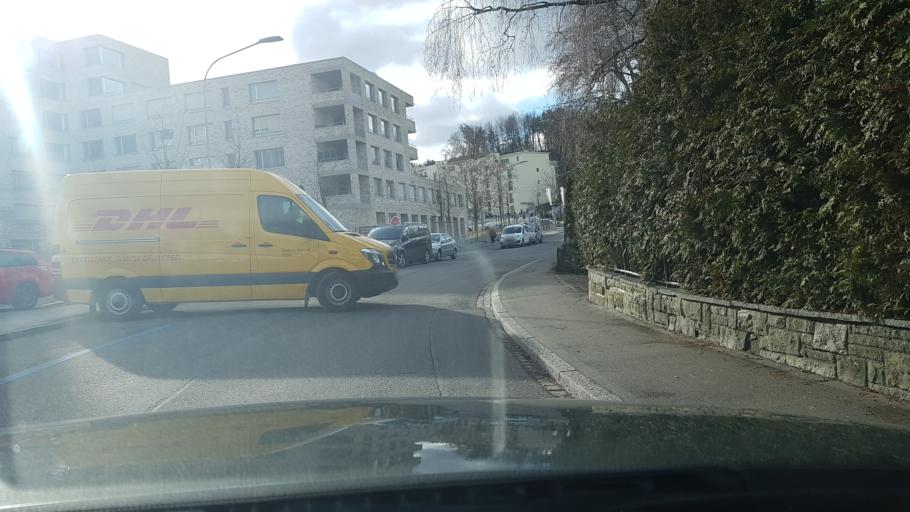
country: CH
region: Zurich
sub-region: Bezirk Zuerich
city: Zuerich (Kreis 12) / Hirzenbach
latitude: 47.3994
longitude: 8.5919
